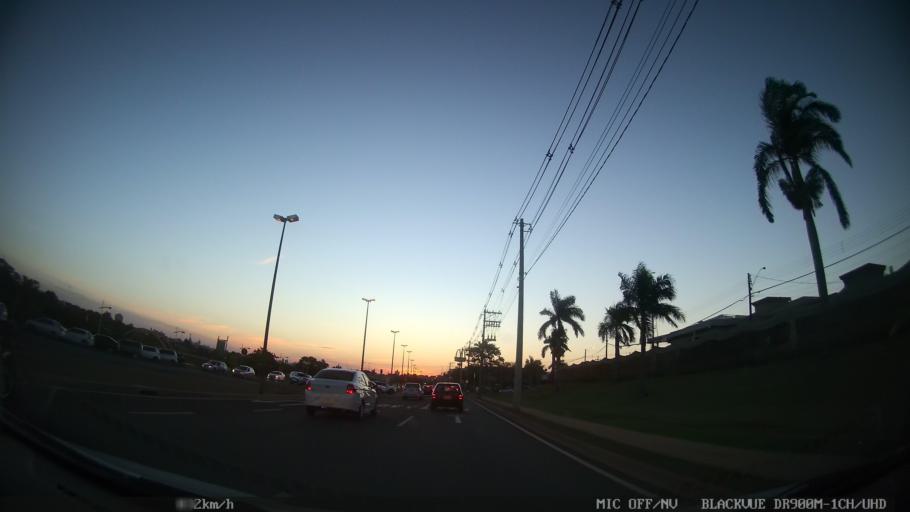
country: BR
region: Sao Paulo
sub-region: Sao Jose Do Rio Preto
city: Sao Jose do Rio Preto
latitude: -20.8106
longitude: -49.3510
